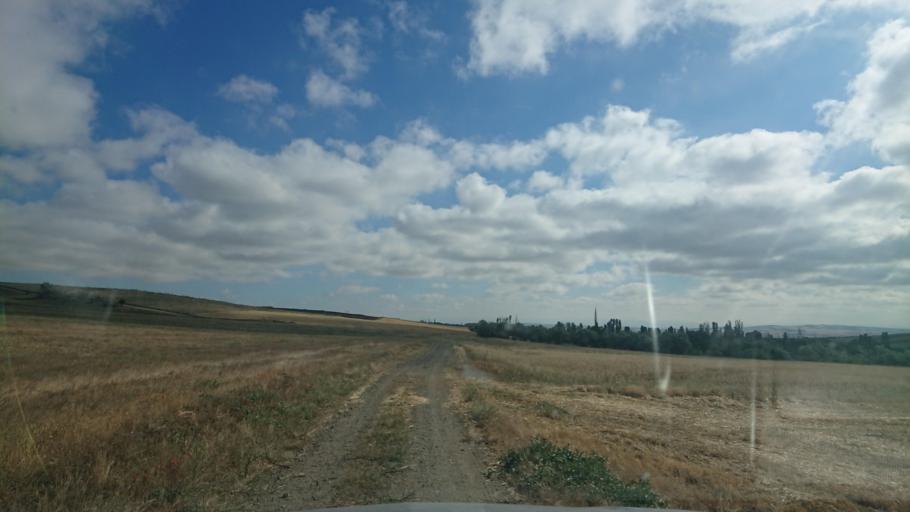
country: TR
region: Aksaray
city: Agacoren
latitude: 38.8532
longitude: 33.9314
